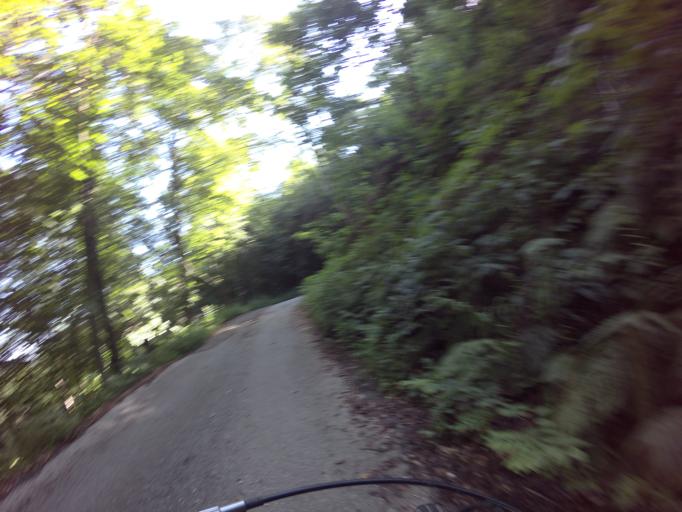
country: IT
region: Piedmont
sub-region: Provincia di Cuneo
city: Chiusa di Pesio
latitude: 44.2819
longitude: 7.6708
